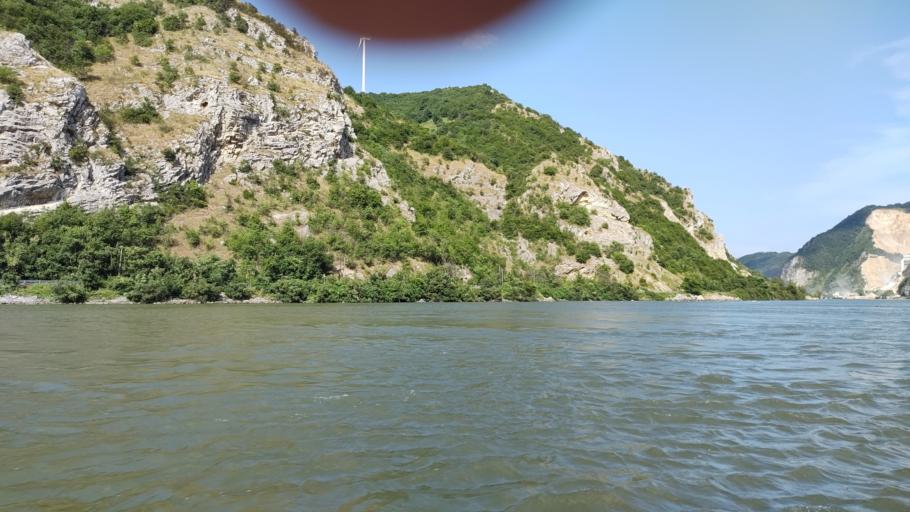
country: RO
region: Caras-Severin
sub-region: Comuna Pescari
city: Coronini
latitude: 44.6566
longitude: 21.7109
